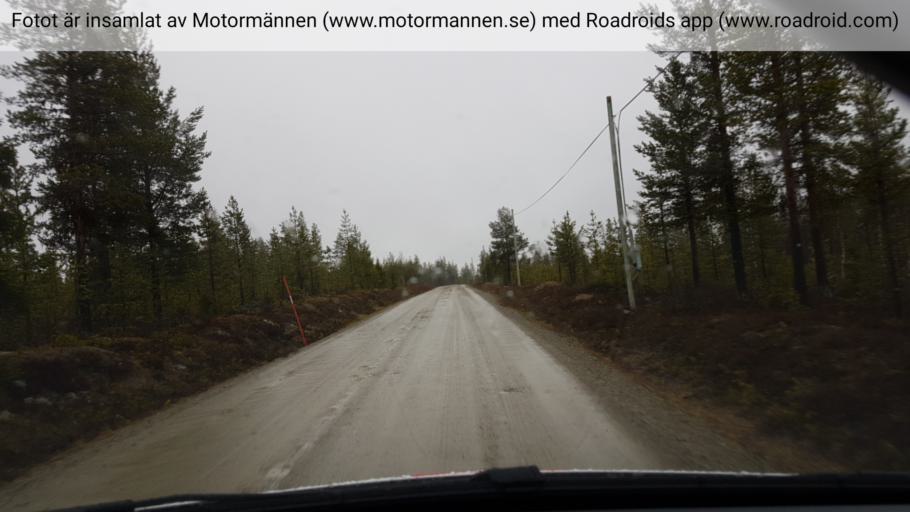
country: SE
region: Jaemtland
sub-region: Are Kommun
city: Jarpen
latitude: 62.5382
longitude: 13.4757
